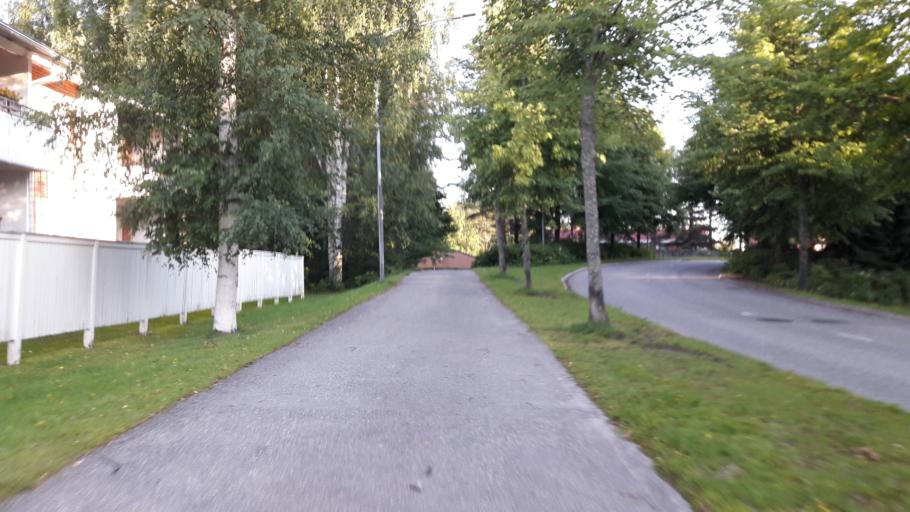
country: FI
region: North Karelia
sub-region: Joensuu
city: Joensuu
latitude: 62.6175
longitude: 29.7092
